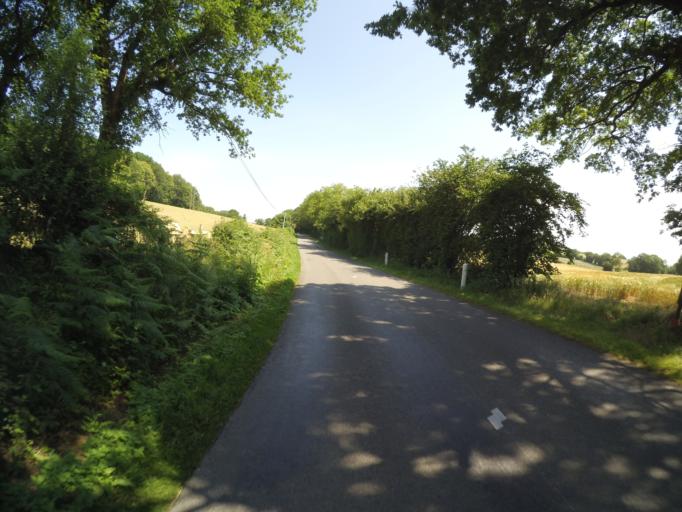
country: FR
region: Pays de la Loire
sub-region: Departement de la Vendee
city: La Flocelliere
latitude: 46.8135
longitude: -0.8540
